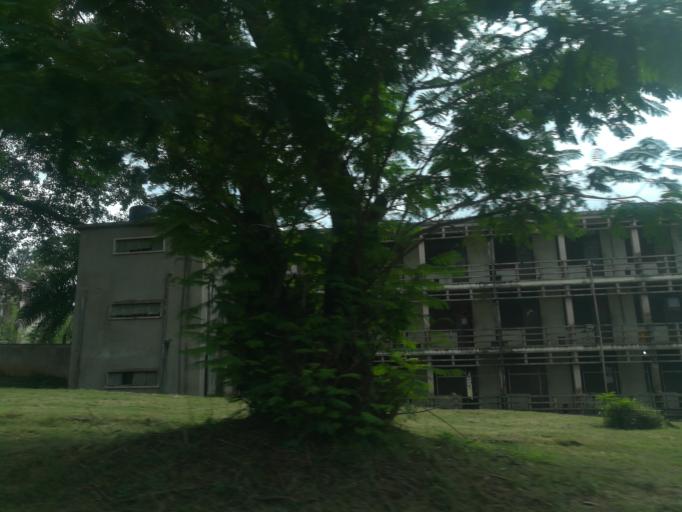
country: NG
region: Oyo
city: Ibadan
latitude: 7.4465
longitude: 3.8989
